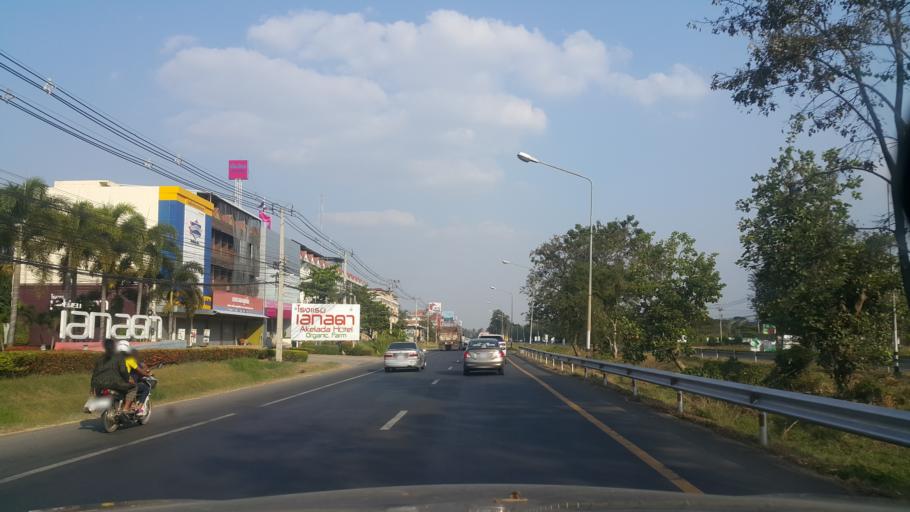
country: TH
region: Buriram
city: Nang Rong
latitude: 14.6331
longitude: 102.8069
